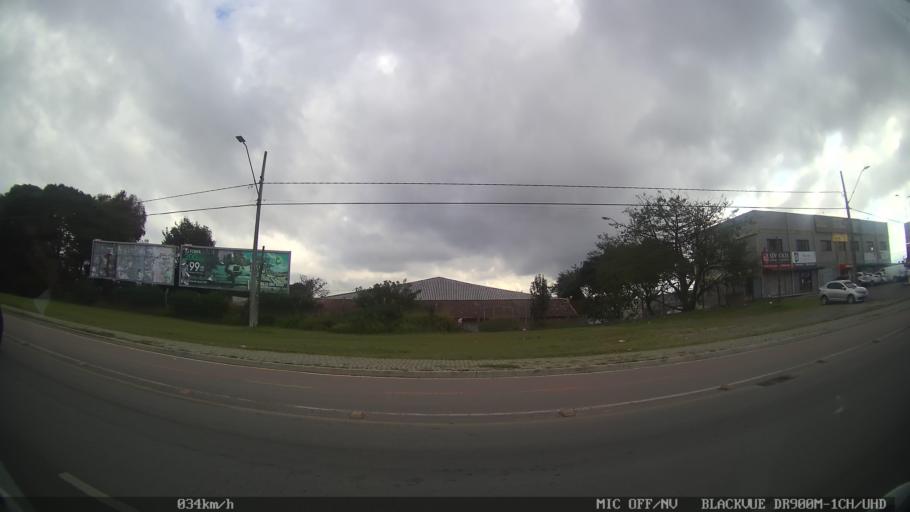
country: BR
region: Parana
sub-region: Pinhais
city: Pinhais
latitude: -25.4243
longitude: -49.1917
